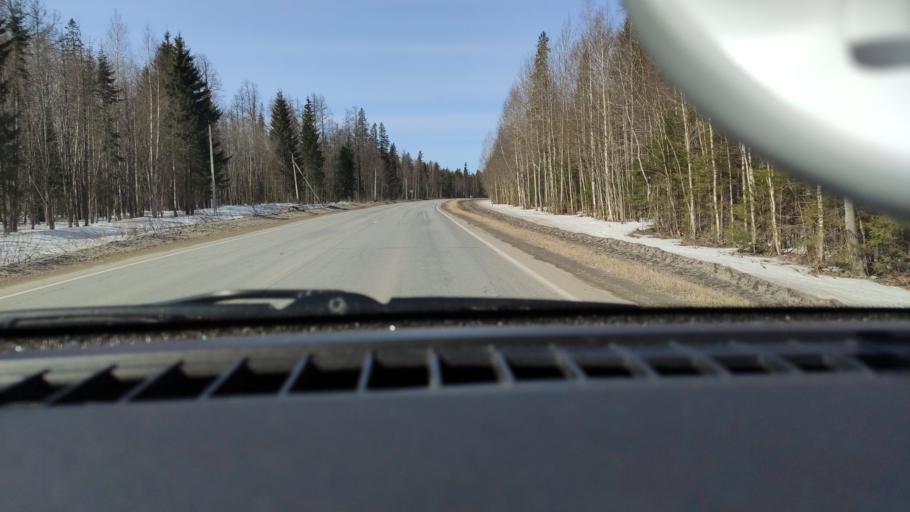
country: RU
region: Perm
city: Perm
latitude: 58.2134
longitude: 56.1797
